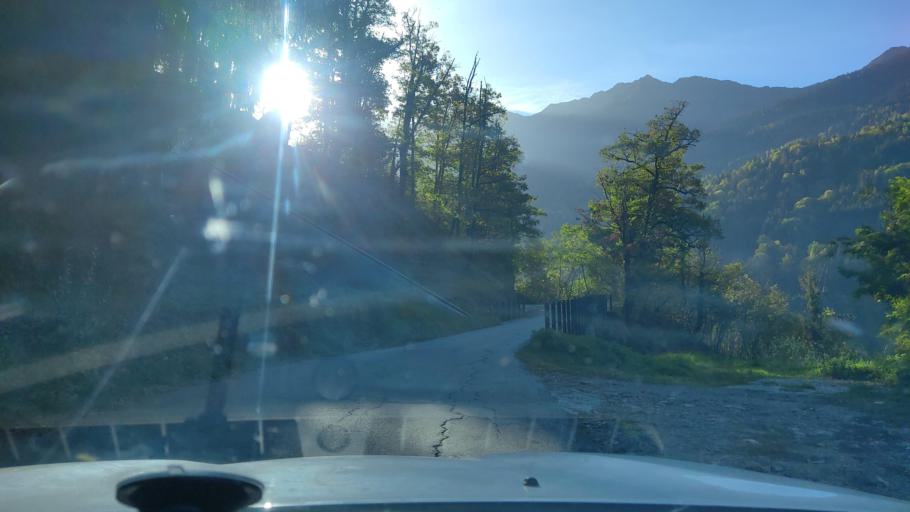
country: FR
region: Rhone-Alpes
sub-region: Departement de la Savoie
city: Marthod
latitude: 45.7193
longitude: 6.4626
